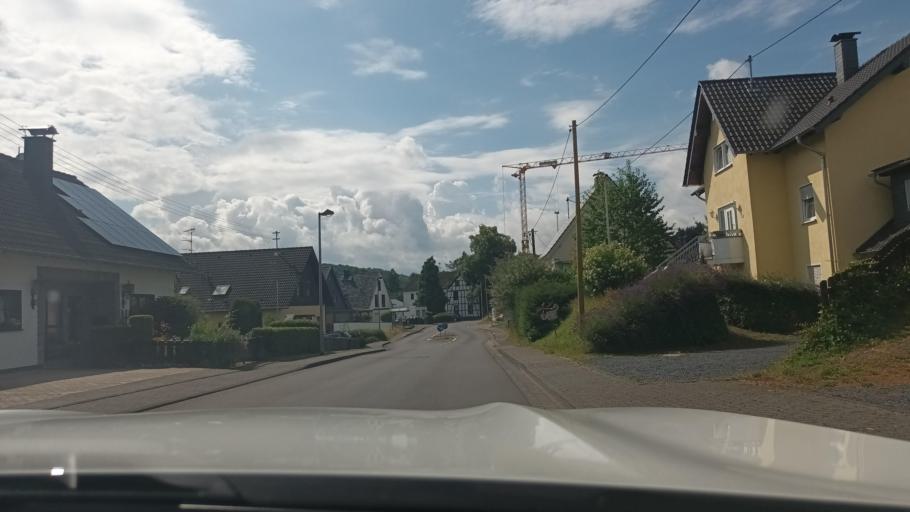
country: DE
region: North Rhine-Westphalia
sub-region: Regierungsbezirk Koln
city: Hennef
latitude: 50.7485
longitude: 7.3096
